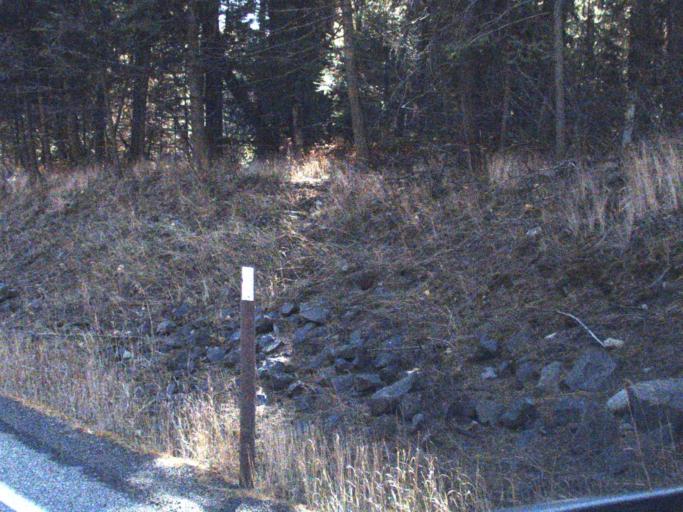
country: US
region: Washington
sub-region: Ferry County
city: Republic
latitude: 48.5989
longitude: -118.6510
